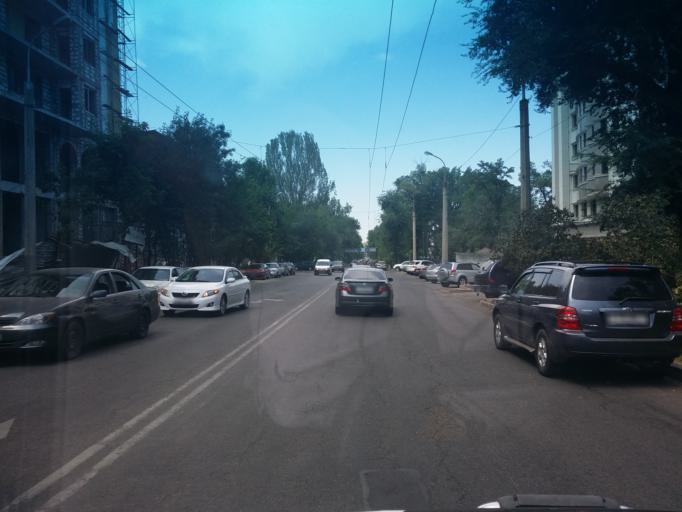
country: KZ
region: Almaty Qalasy
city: Almaty
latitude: 43.2439
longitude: 76.9338
